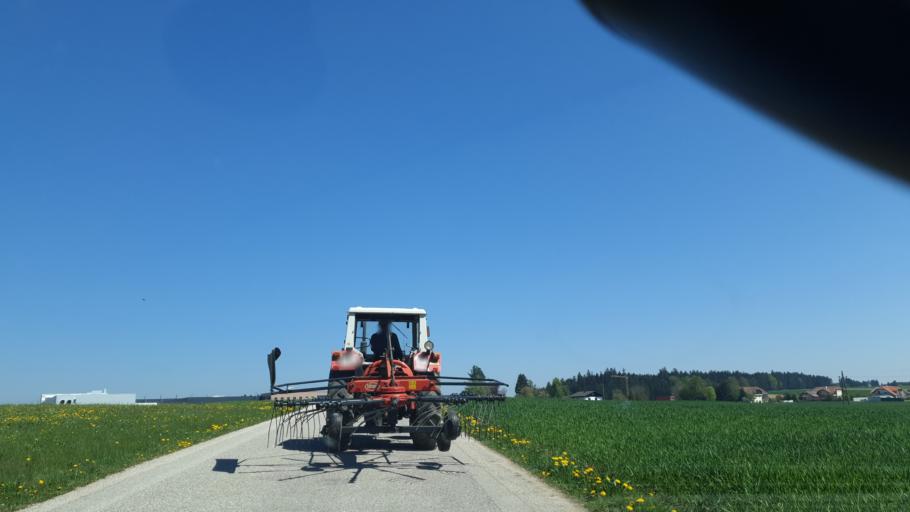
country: AT
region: Upper Austria
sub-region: Politischer Bezirk Vocklabruck
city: Gampern
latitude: 47.9988
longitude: 13.5597
